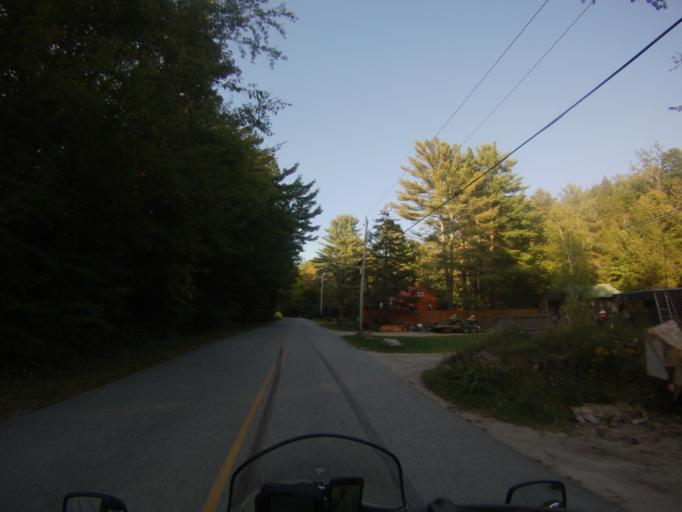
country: US
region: Vermont
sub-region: Addison County
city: Middlebury (village)
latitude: 43.9914
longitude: -73.0321
